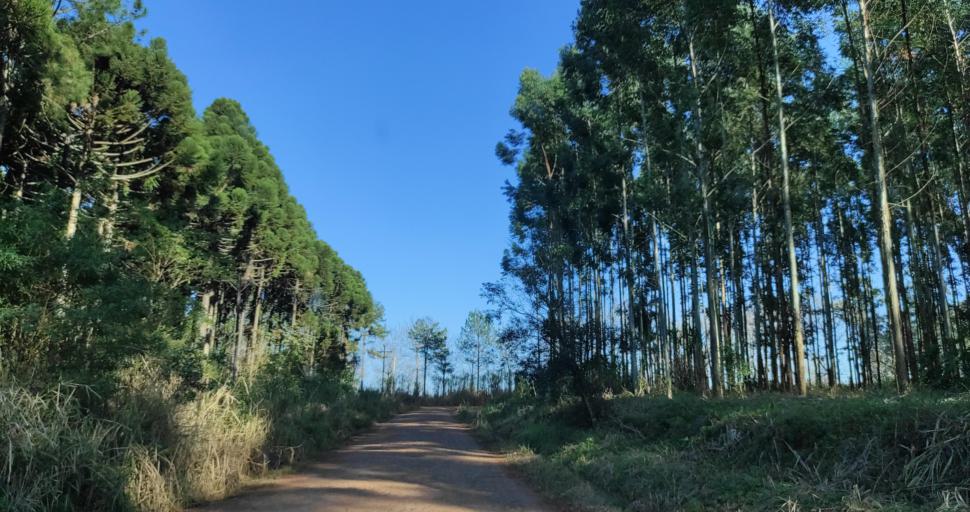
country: AR
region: Misiones
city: Puerto Rico
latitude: -26.8618
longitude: -55.0255
